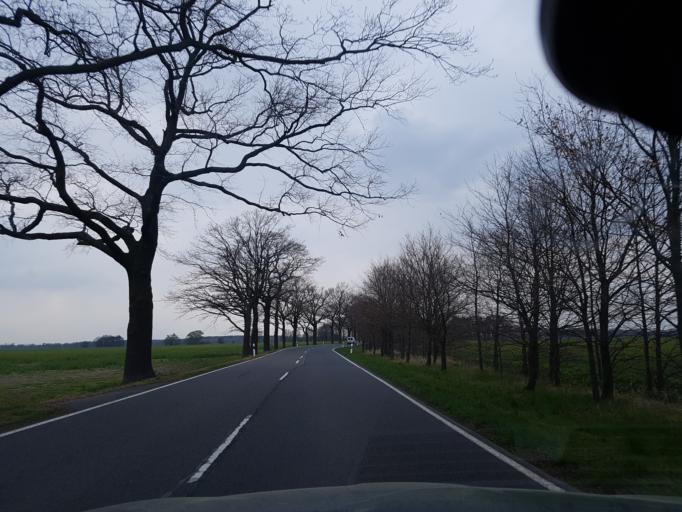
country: DE
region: Brandenburg
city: Schraden
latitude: 51.4051
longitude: 13.6981
